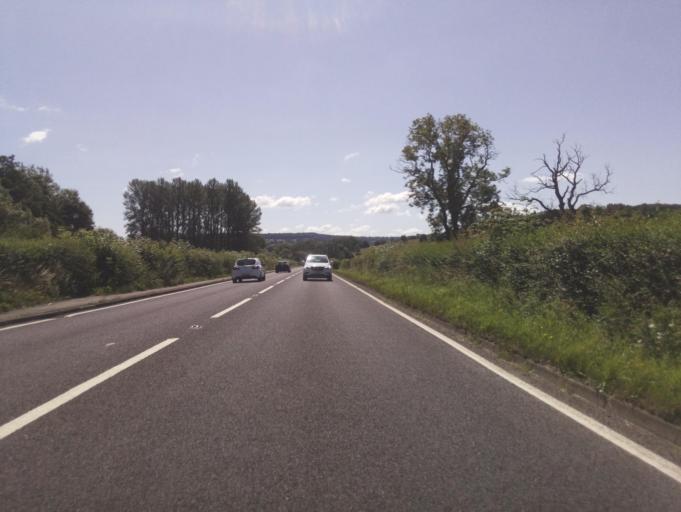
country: GB
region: England
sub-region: Derbyshire
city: Bakewell
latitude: 53.2008
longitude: -1.6624
